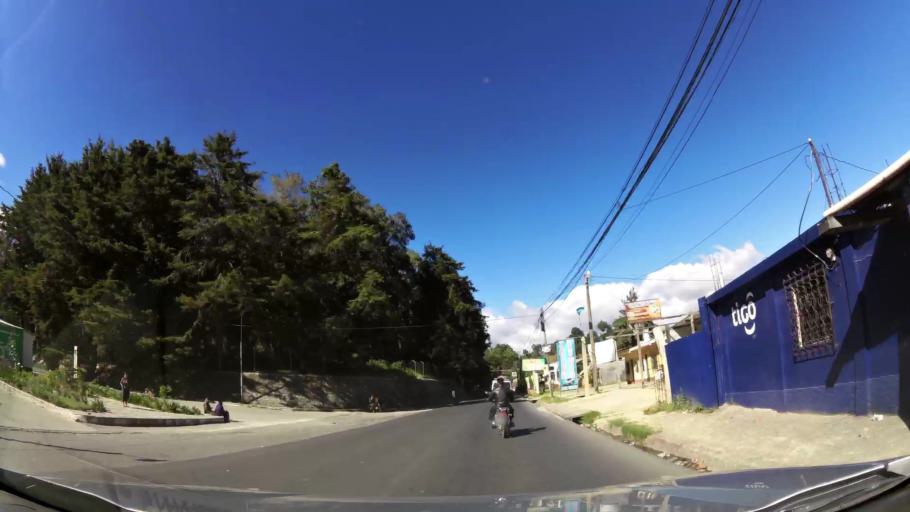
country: GT
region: Solola
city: Solola
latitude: 14.7893
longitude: -91.1828
